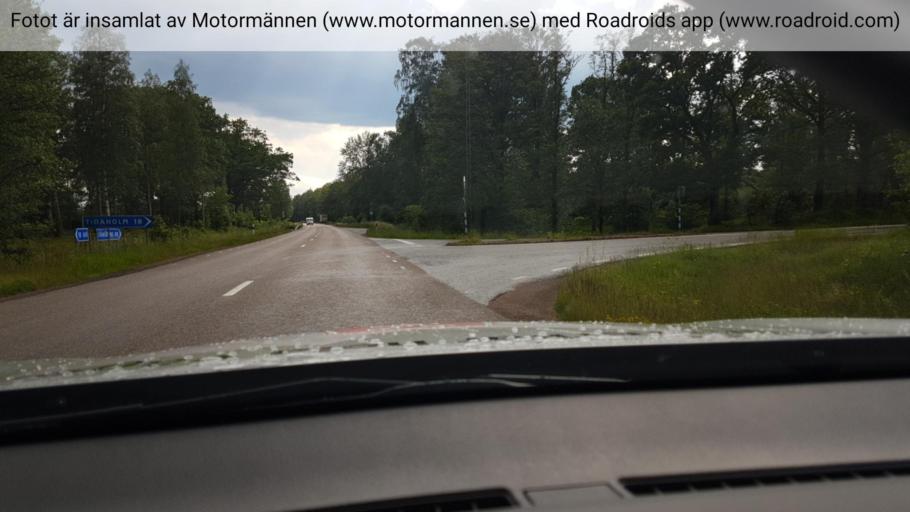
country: SE
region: Vaestra Goetaland
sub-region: Hjo Kommun
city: Hjo
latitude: 58.2261
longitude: 14.2110
